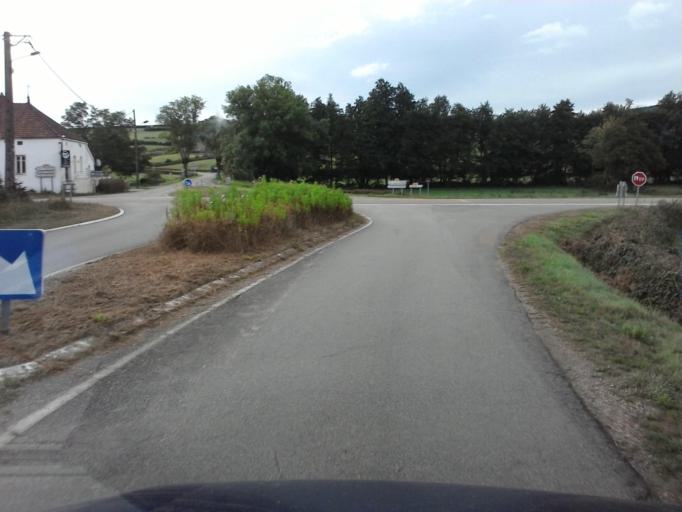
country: FR
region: Bourgogne
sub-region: Departement de la Nievre
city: Lormes
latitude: 47.2294
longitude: 3.8259
